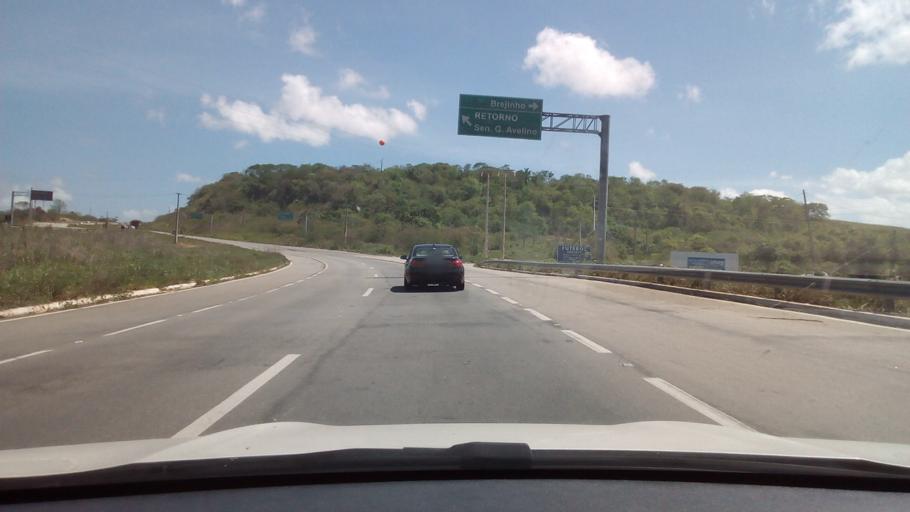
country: BR
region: Rio Grande do Norte
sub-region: Nisia Floresta
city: Nisia Floresta
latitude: -6.1144
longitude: -35.2334
